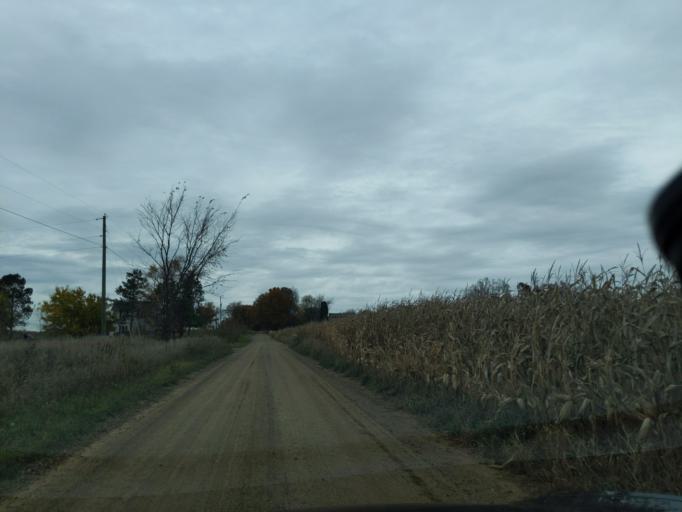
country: US
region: Michigan
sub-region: Eaton County
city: Eaton Rapids
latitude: 42.4271
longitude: -84.6005
